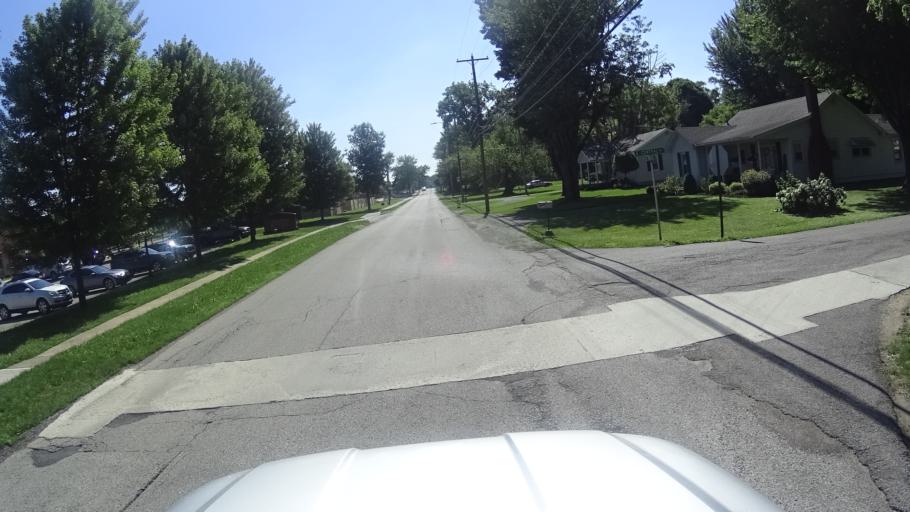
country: US
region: Indiana
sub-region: Madison County
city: Pendleton
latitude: 40.0037
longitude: -85.7357
